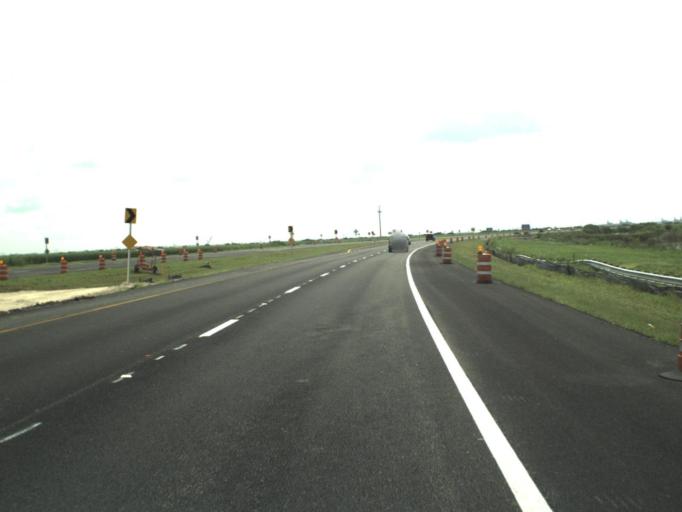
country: US
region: Florida
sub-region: Palm Beach County
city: Loxahatchee Groves
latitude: 26.7253
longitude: -80.4444
